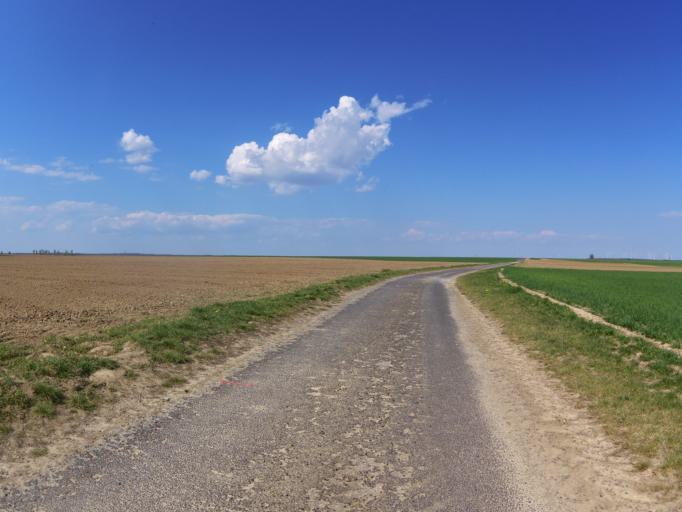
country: DE
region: Bavaria
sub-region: Regierungsbezirk Unterfranken
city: Oberpleichfeld
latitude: 49.8472
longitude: 10.0879
